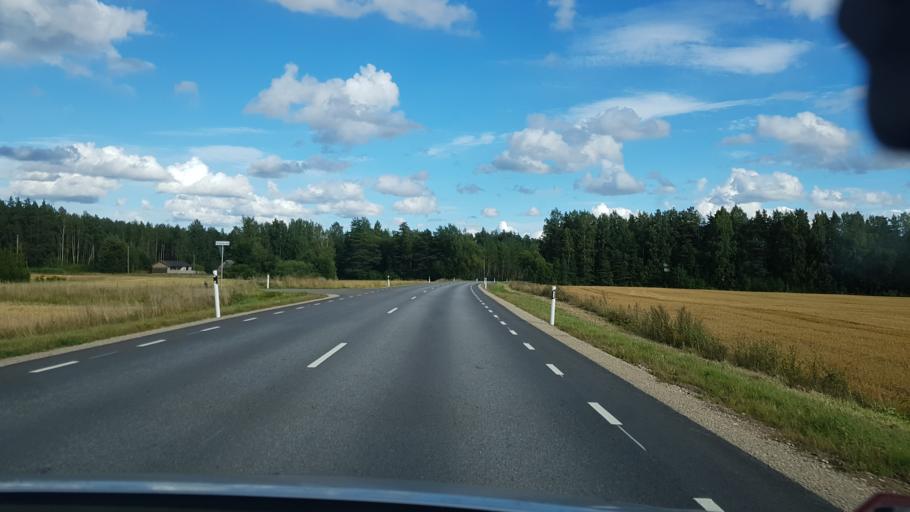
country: EE
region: Polvamaa
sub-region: Polva linn
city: Polva
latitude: 58.0756
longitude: 27.2556
